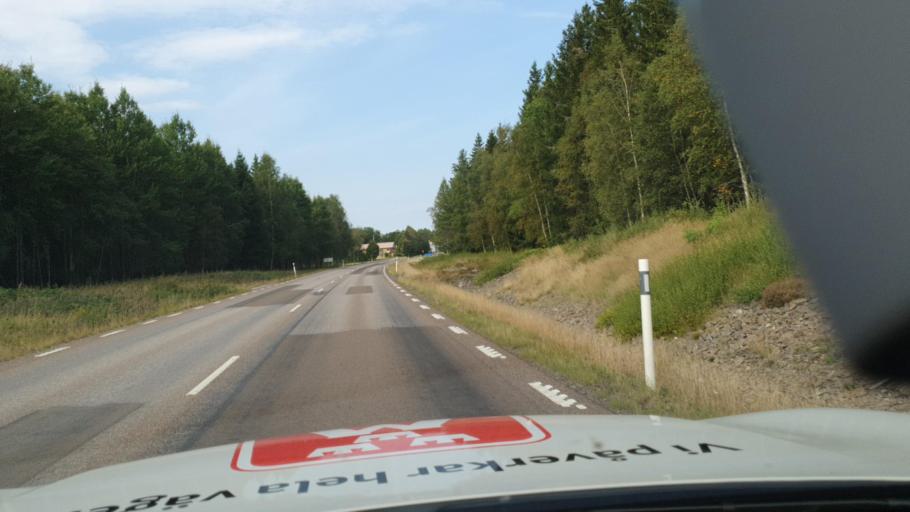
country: SE
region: Vaestra Goetaland
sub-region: Melleruds Kommun
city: Mellerud
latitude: 58.7478
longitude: 12.2979
